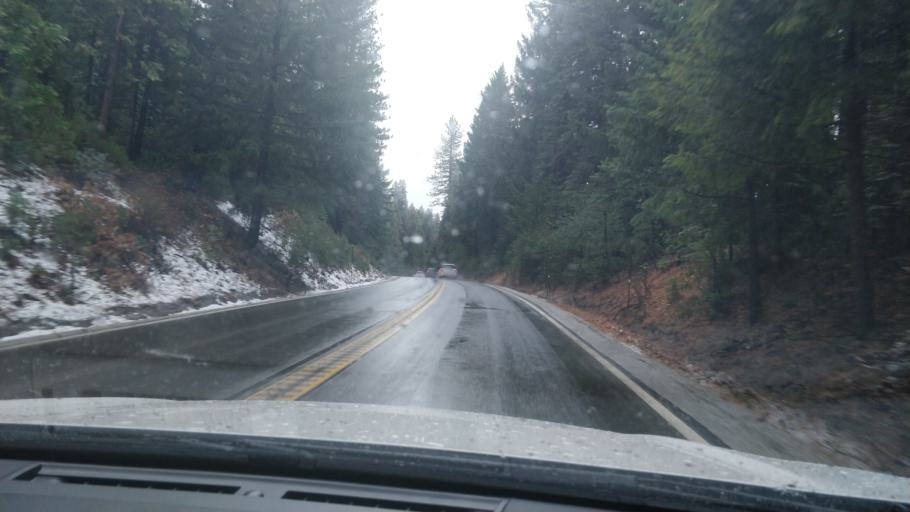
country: US
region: California
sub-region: Nevada County
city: Nevada City
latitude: 39.3128
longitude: -120.7804
